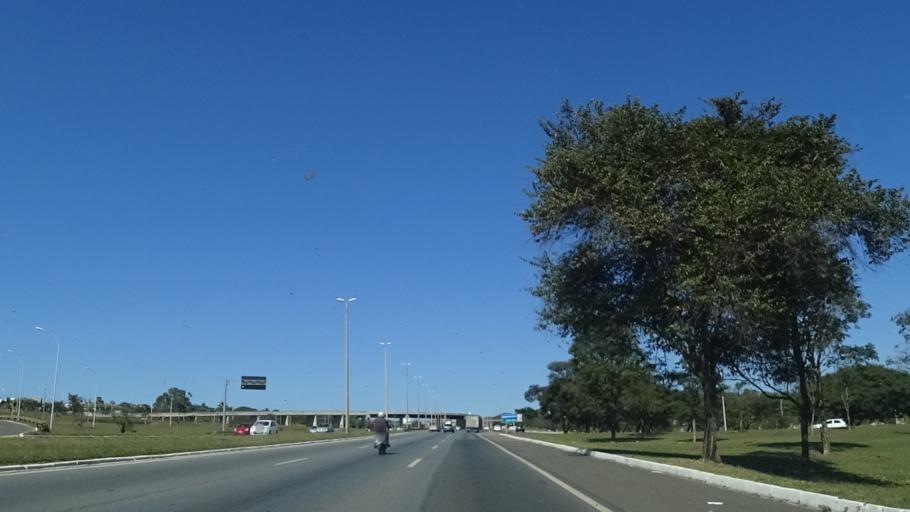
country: BR
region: Federal District
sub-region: Brasilia
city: Brasilia
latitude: -15.8725
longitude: -47.9585
